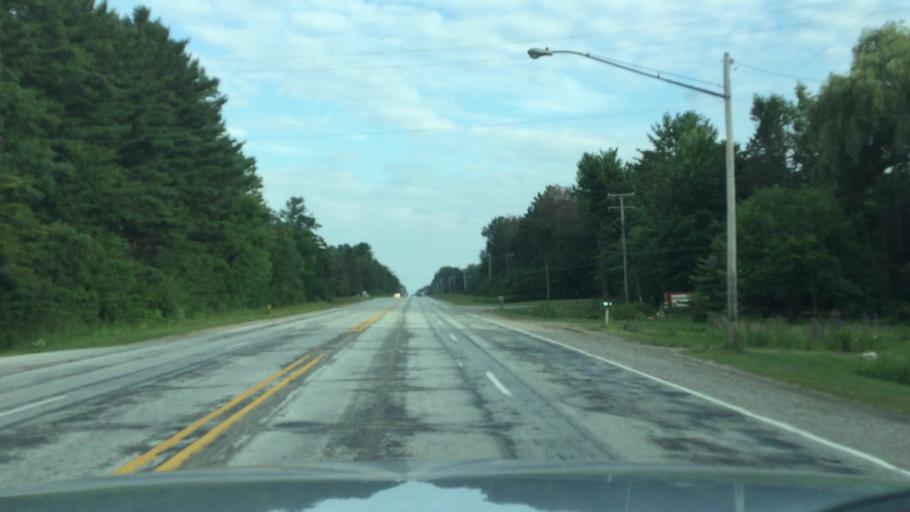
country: US
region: Michigan
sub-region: Saginaw County
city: Birch Run
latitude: 43.3170
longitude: -83.8200
